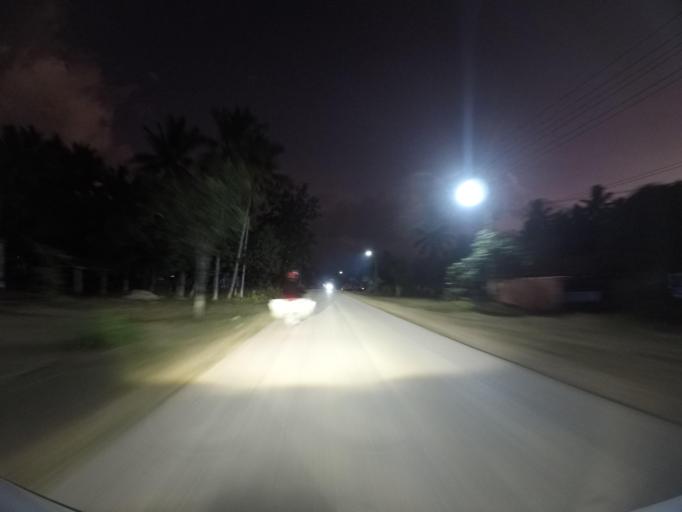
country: TL
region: Lautem
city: Lospalos
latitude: -8.4697
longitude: 126.9932
